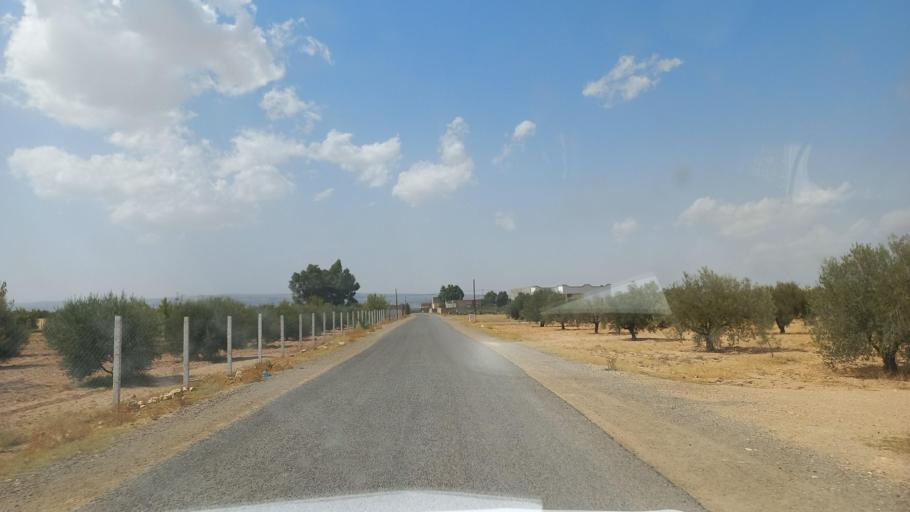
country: TN
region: Al Qasrayn
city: Kasserine
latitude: 35.2501
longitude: 9.0203
